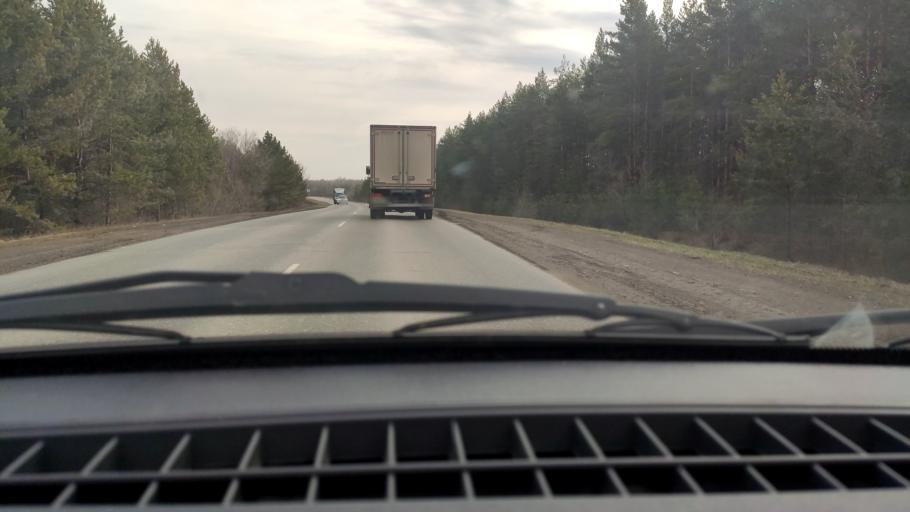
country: RU
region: Bashkortostan
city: Davlekanovo
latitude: 54.2446
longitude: 55.0733
